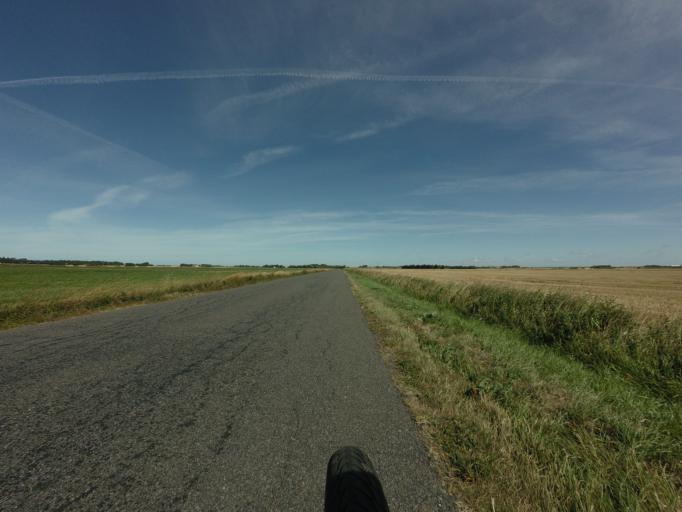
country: DK
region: North Denmark
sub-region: Bronderslev Kommune
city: Bronderslev
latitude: 57.3116
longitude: 9.8111
